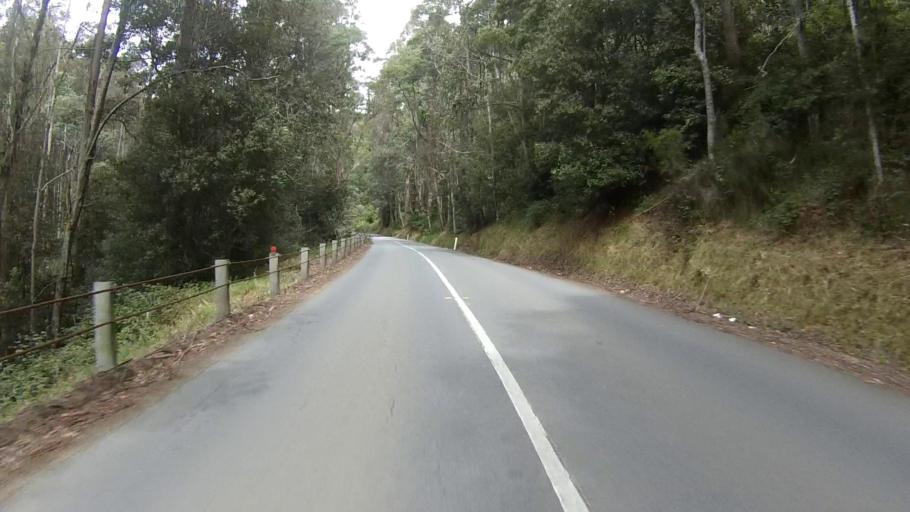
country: AU
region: Tasmania
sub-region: Kingborough
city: Kettering
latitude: -43.1263
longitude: 147.1794
